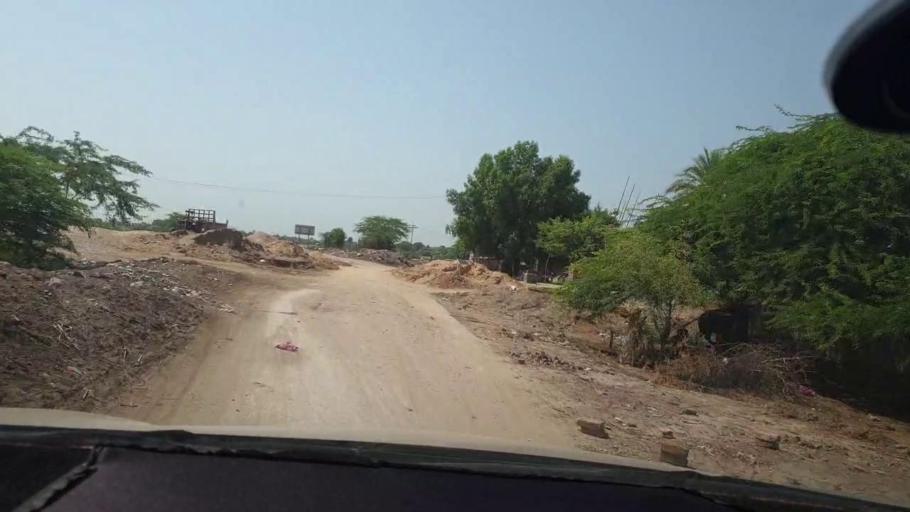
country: PK
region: Sindh
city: Kambar
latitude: 27.5056
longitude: 68.0116
